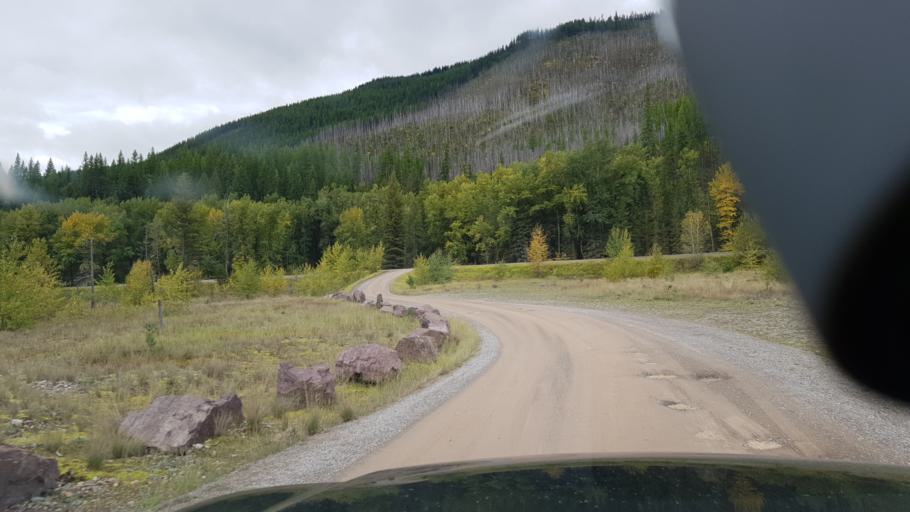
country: US
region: Montana
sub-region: Flathead County
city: Columbia Falls
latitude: 48.5687
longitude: -114.1307
